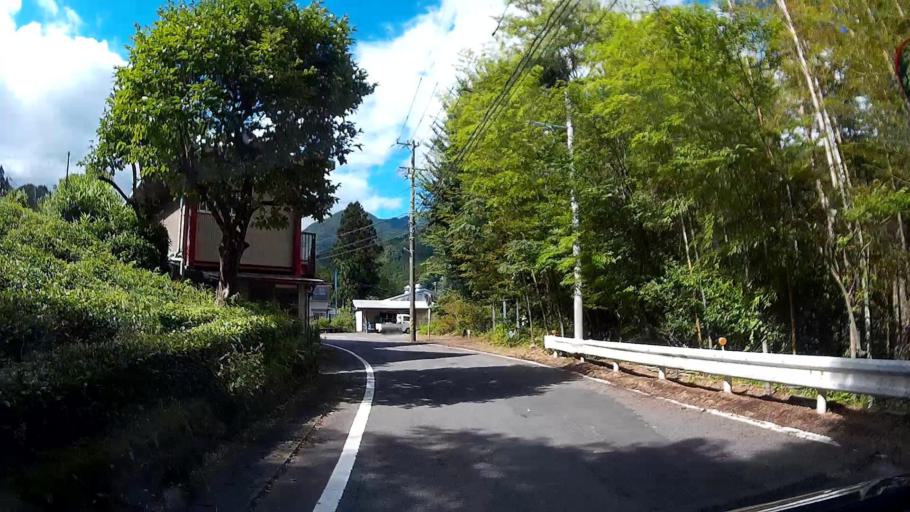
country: JP
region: Shizuoka
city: Shizuoka-shi
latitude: 35.2487
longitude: 138.2425
